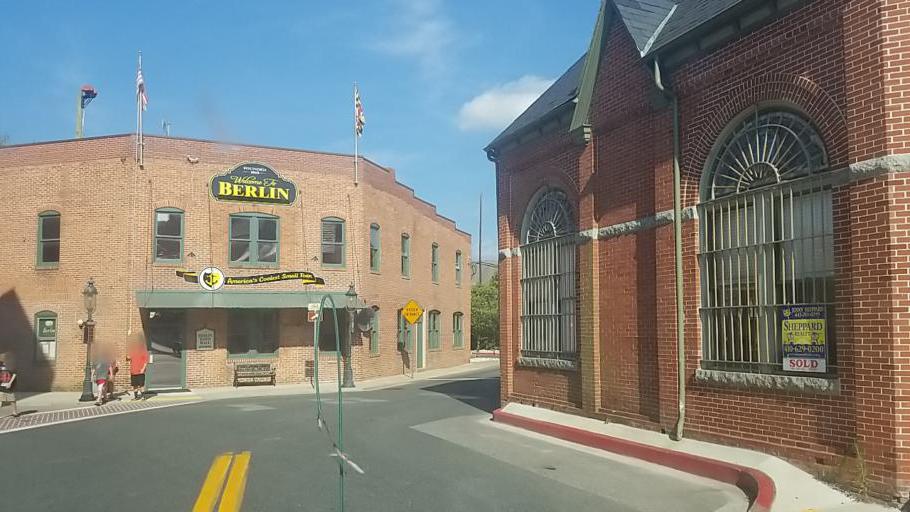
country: US
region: Maryland
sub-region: Worcester County
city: Berlin
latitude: 38.3245
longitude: -75.2189
